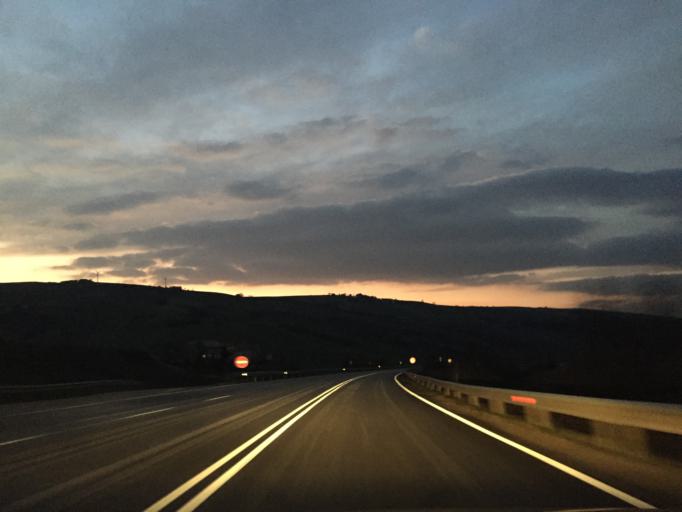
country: IT
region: Apulia
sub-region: Provincia di Foggia
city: Volturara Appula
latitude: 41.4565
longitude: 15.0654
